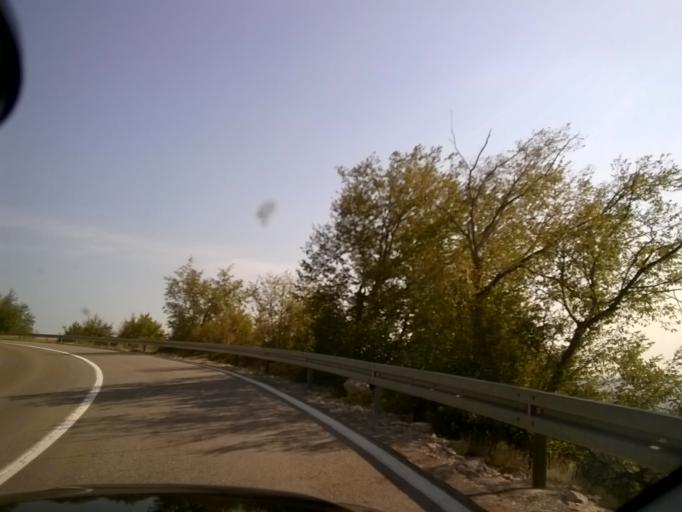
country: HR
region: Licko-Senjska
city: Karlobag
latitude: 44.5259
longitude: 15.0958
